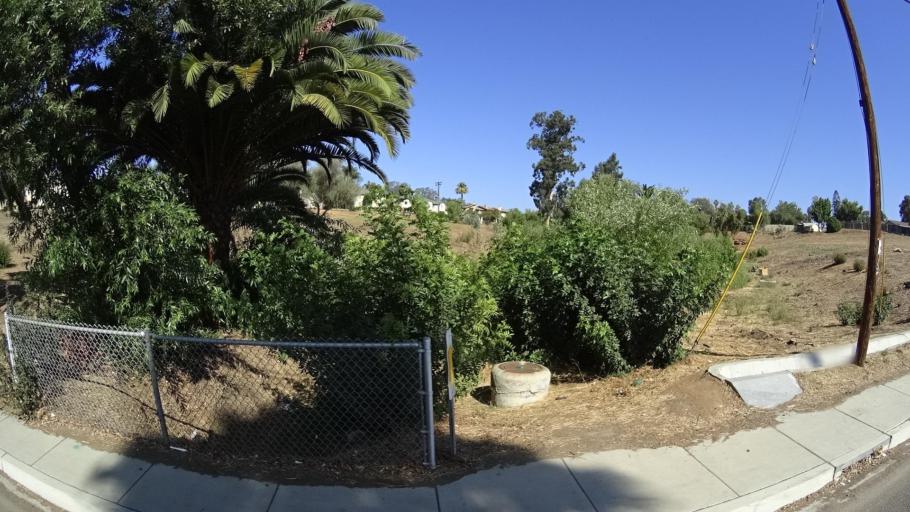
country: US
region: California
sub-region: San Diego County
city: Fallbrook
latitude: 33.3737
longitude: -117.2567
